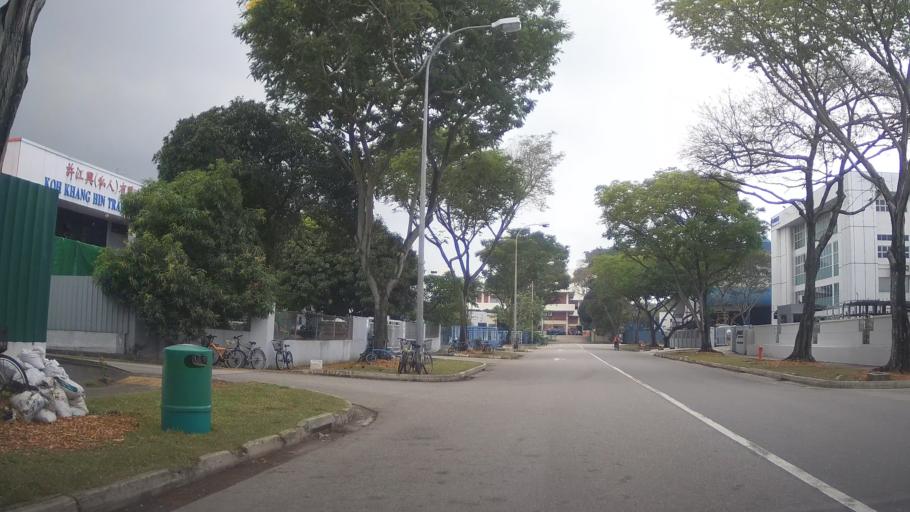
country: MY
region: Johor
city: Johor Bahru
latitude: 1.3306
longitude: 103.6913
